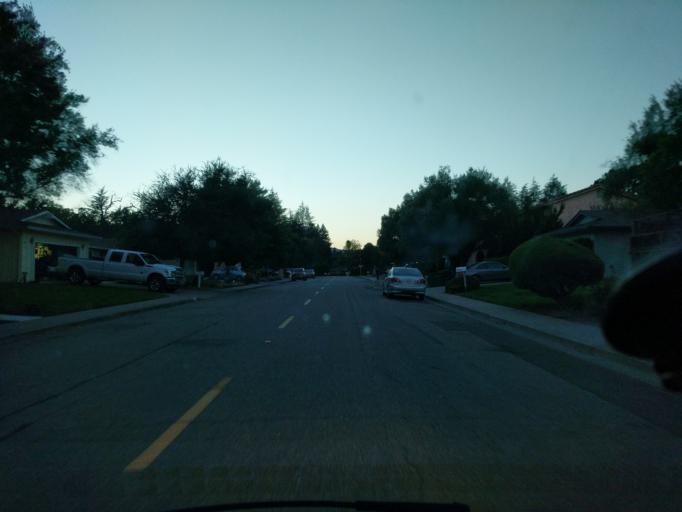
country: US
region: California
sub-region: Contra Costa County
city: San Ramon
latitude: 37.7679
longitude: -121.9808
